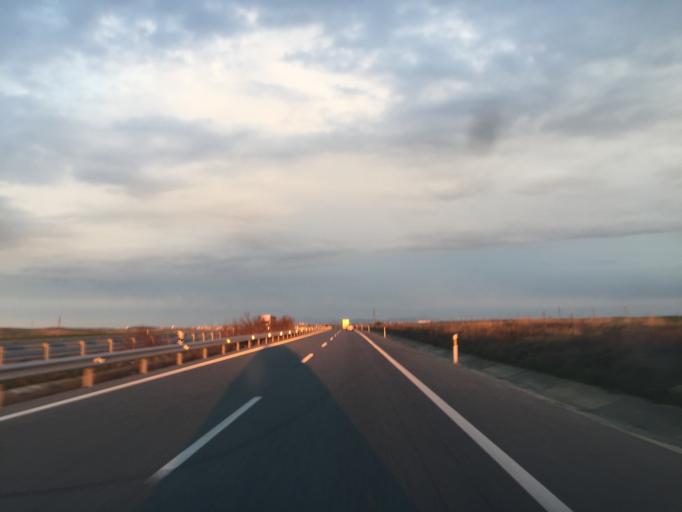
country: ES
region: Castille and Leon
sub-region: Provincia de Burgos
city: Albillos
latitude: 42.3053
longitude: -3.7799
